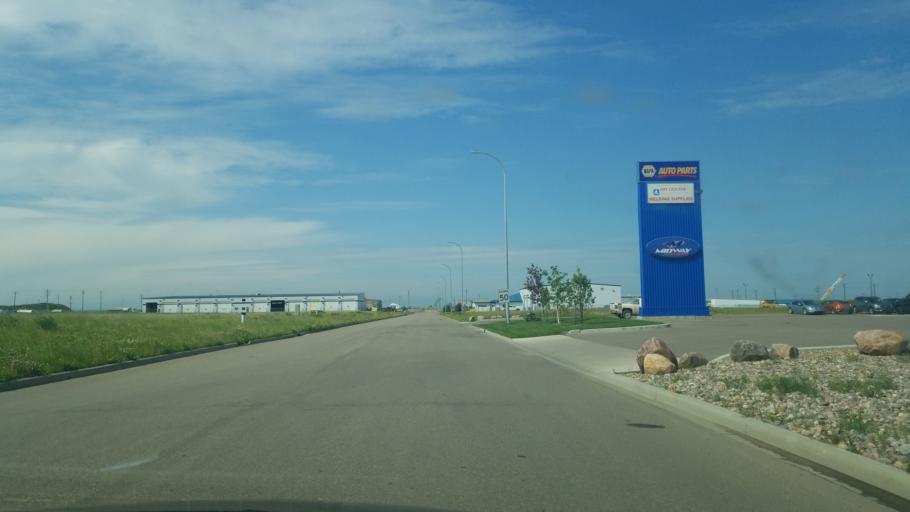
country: CA
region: Saskatchewan
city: Lloydminster
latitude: 53.2873
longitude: -110.0419
